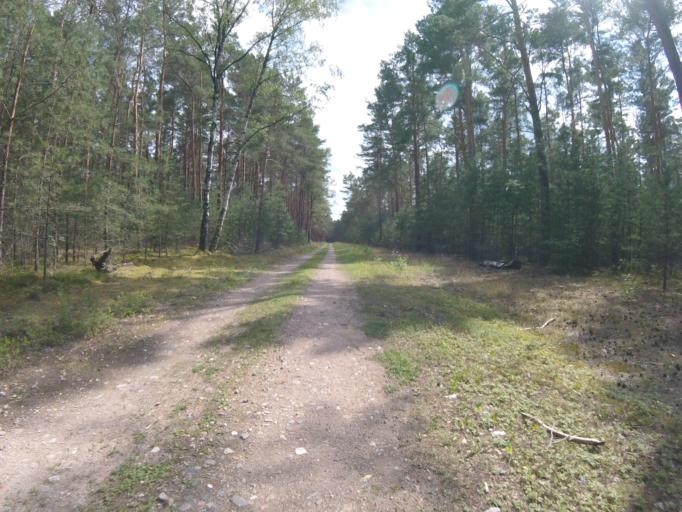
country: DE
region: Brandenburg
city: Halbe
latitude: 52.1255
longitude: 13.6966
